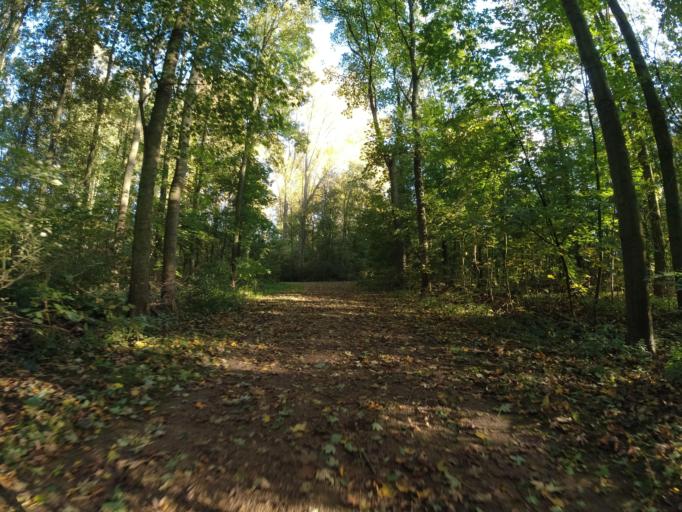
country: DE
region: North Rhine-Westphalia
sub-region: Regierungsbezirk Dusseldorf
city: Hochfeld
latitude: 51.4098
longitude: 6.7004
